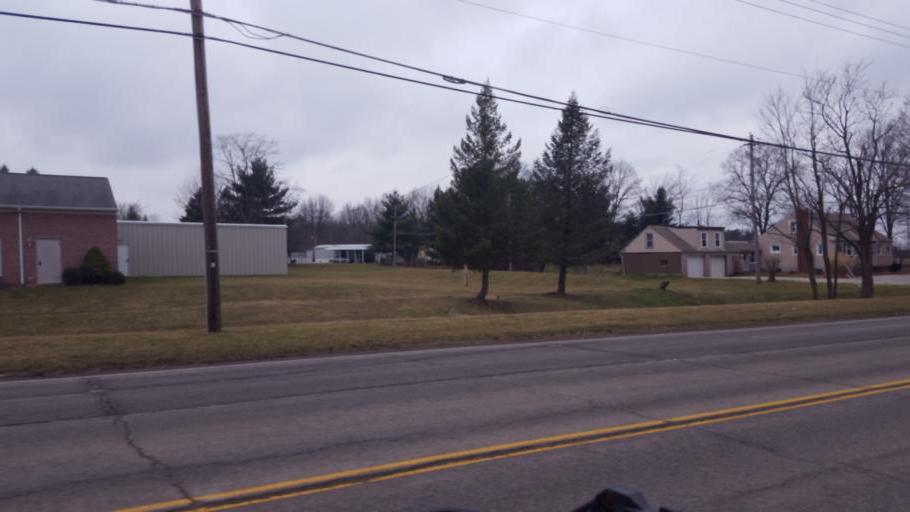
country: US
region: Ohio
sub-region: Richland County
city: Ontario
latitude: 40.8046
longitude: -82.5901
